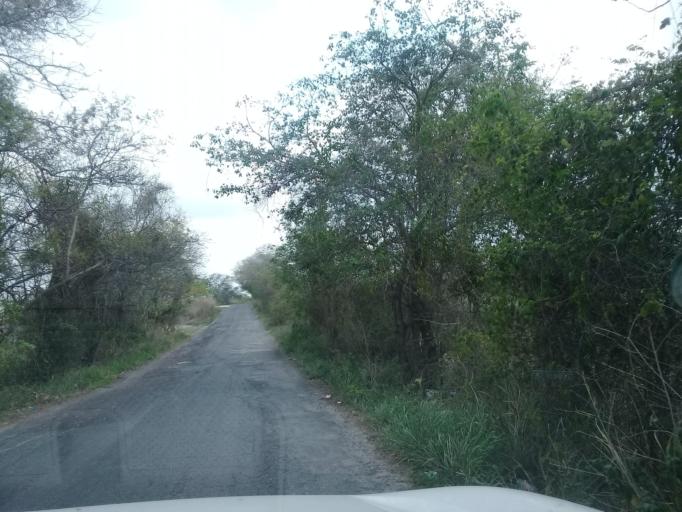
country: MX
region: Veracruz
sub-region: Emiliano Zapata
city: Plan del Rio
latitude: 19.3546
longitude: -96.6586
